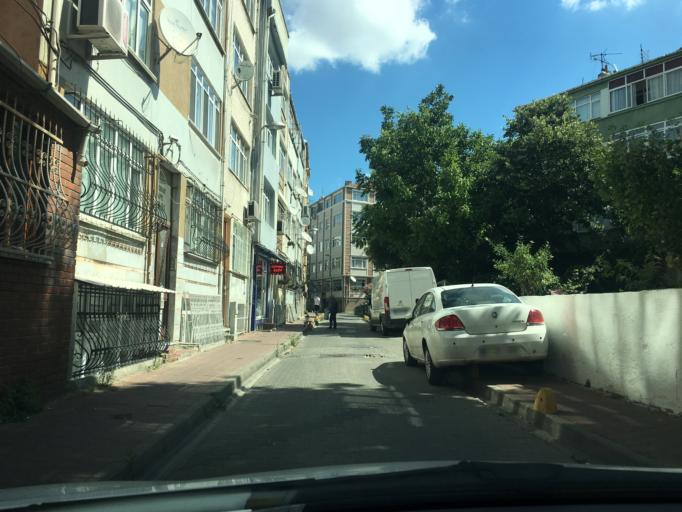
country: TR
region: Istanbul
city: Istanbul
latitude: 41.0097
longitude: 28.9299
